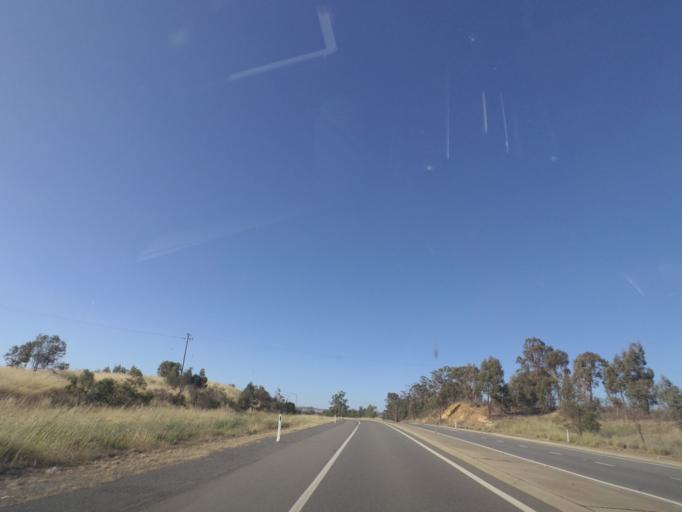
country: AU
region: New South Wales
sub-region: Wagga Wagga
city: Forest Hill
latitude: -35.2668
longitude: 147.7460
